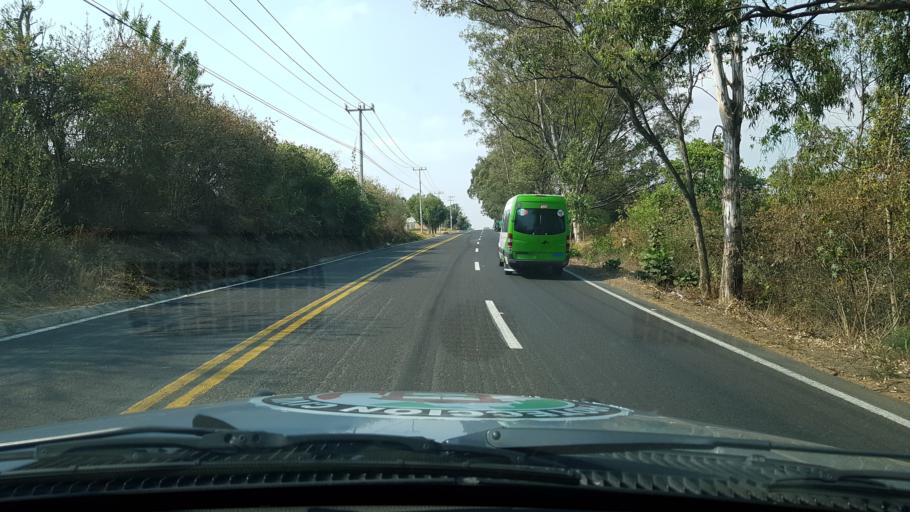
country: MX
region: Mexico
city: Tepetlixpa
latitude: 19.0100
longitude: -98.8240
